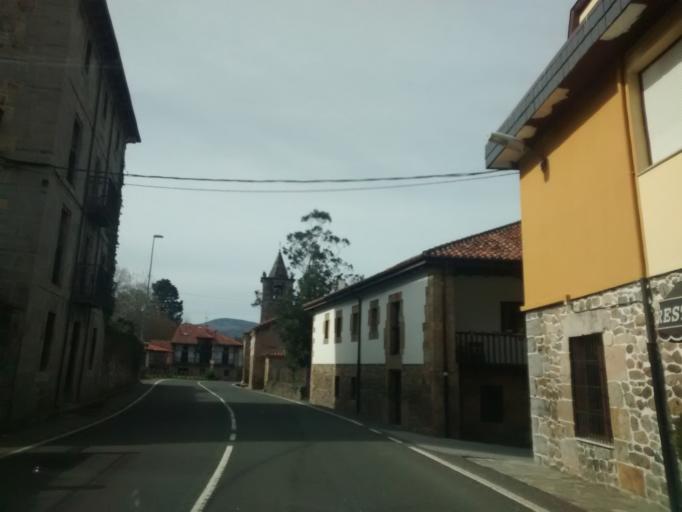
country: ES
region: Cantabria
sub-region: Provincia de Cantabria
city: Santiurde de Toranzo
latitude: 43.1920
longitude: -3.9152
